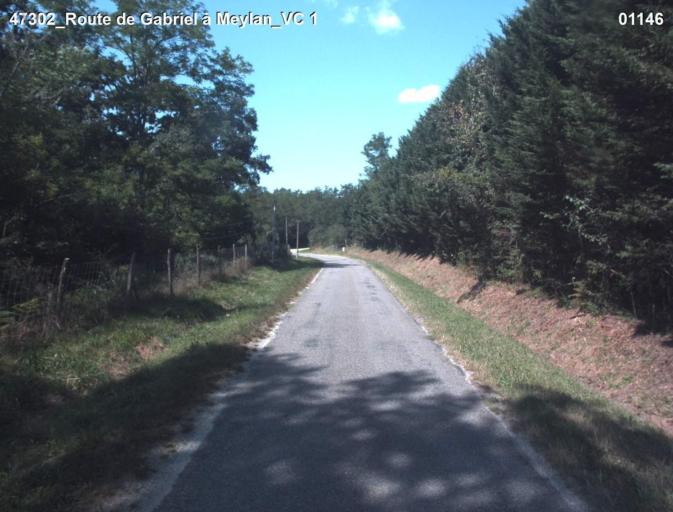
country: FR
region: Aquitaine
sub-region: Departement du Lot-et-Garonne
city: Mezin
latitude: 44.0620
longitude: 0.1433
